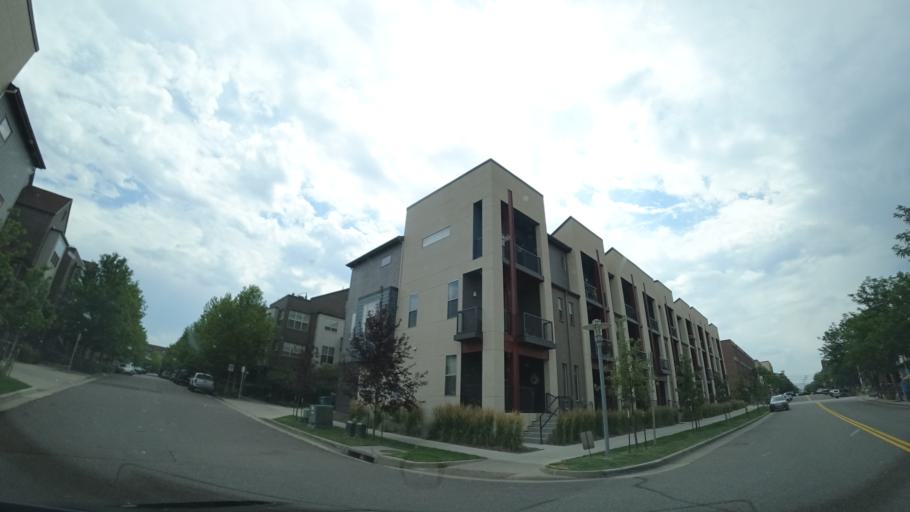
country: US
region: Colorado
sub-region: Jefferson County
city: Lakewood
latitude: 39.7093
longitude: -105.0741
